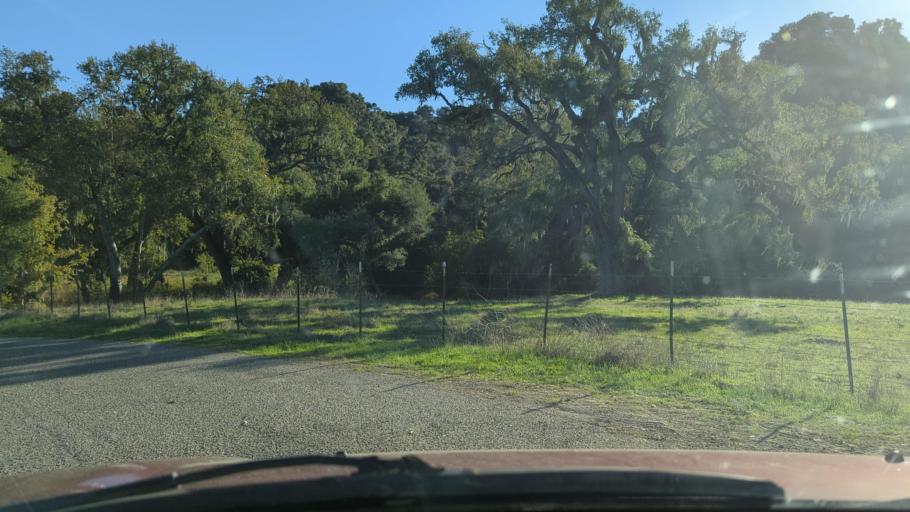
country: US
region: California
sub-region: Santa Barbara County
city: Santa Ynez
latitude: 34.5704
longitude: -120.0975
